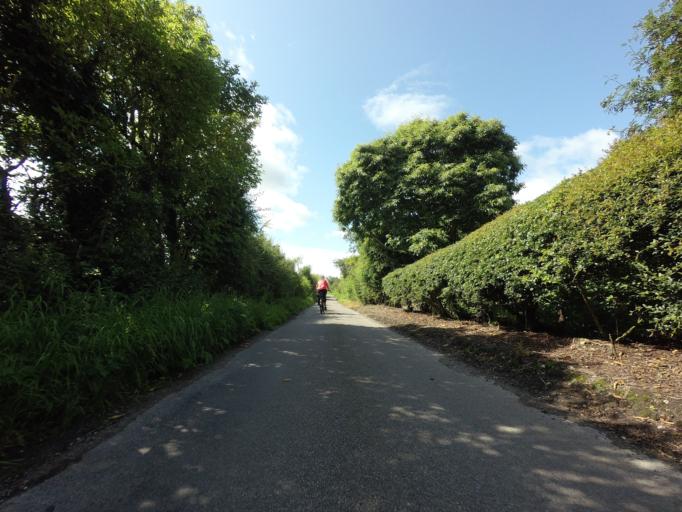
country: GB
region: Scotland
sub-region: Moray
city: Kinloss
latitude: 57.6450
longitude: -3.5213
